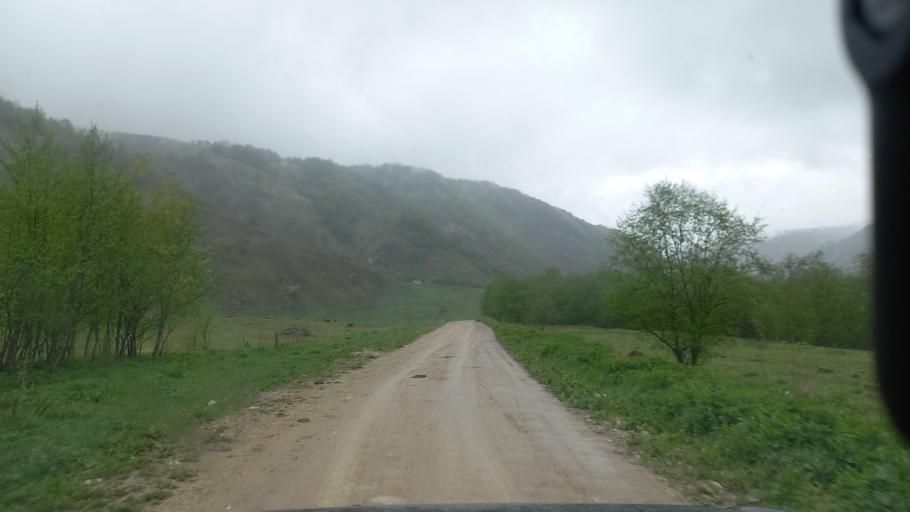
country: RU
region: Kabardino-Balkariya
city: Gundelen
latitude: 43.5847
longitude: 43.0879
